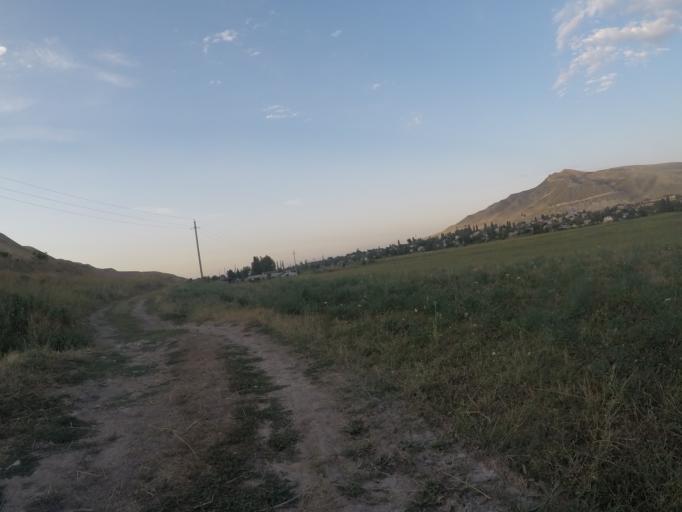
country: KG
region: Chuy
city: Bishkek
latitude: 42.7621
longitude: 74.6371
